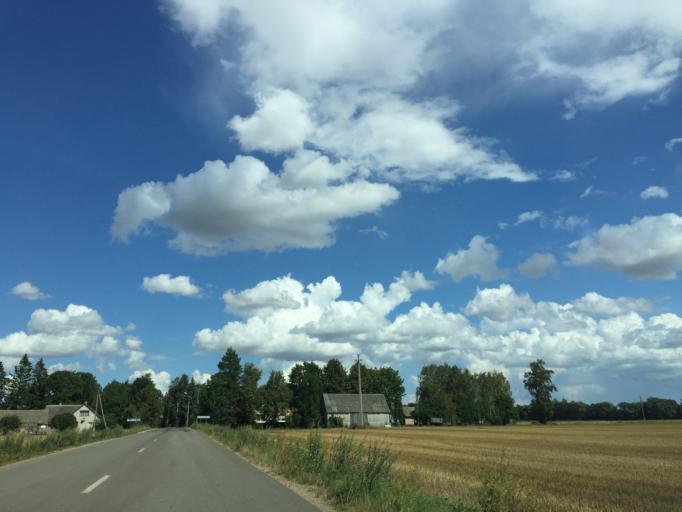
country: LV
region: Rundales
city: Pilsrundale
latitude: 56.3110
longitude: 23.9092
